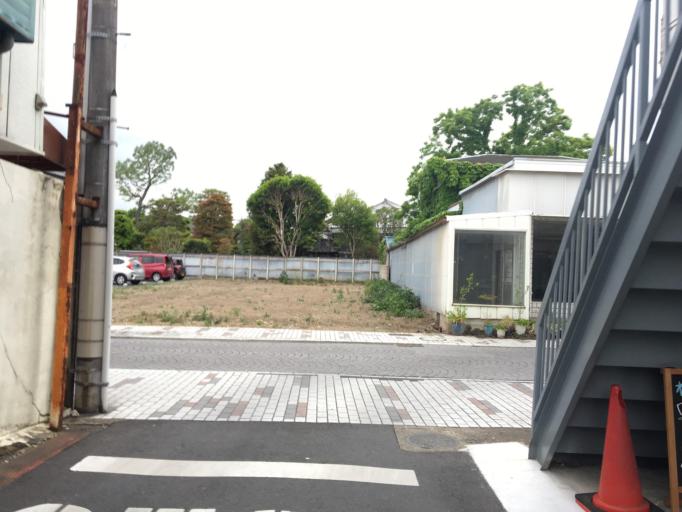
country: JP
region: Tochigi
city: Tochigi
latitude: 36.3781
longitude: 139.7318
